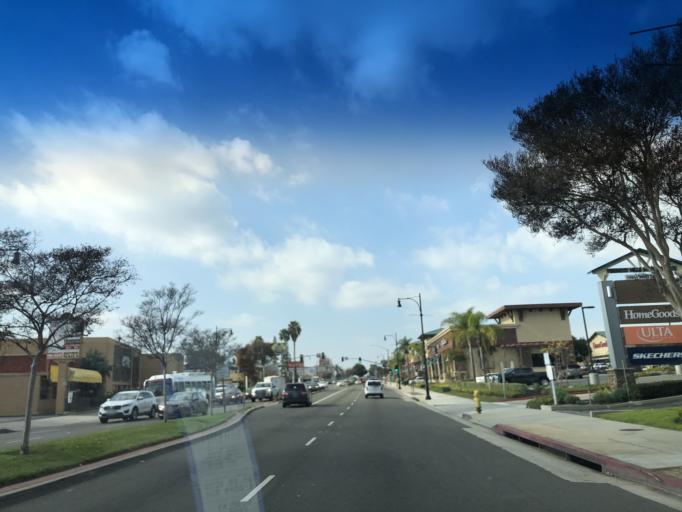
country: US
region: California
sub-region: Los Angeles County
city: East La Mirada
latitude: 33.9468
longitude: -117.9994
